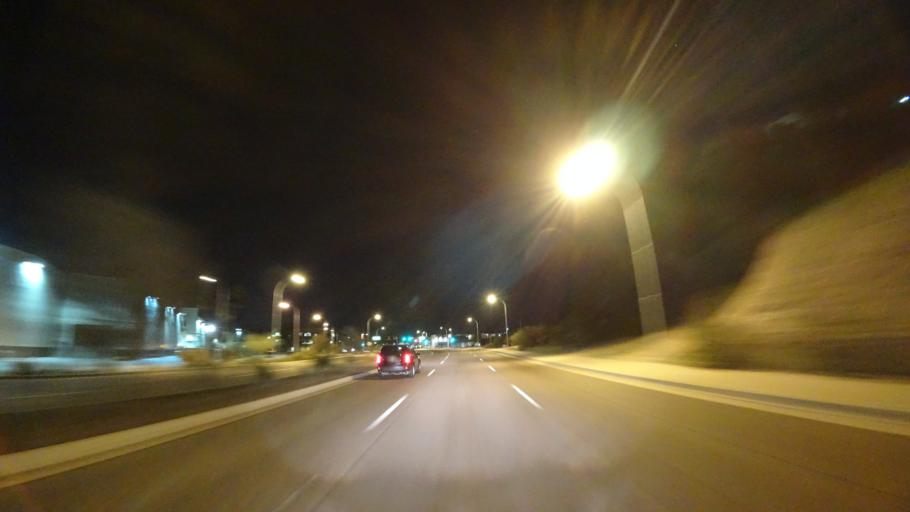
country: US
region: Arizona
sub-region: Maricopa County
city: Tempe Junction
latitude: 33.4083
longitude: -111.9677
